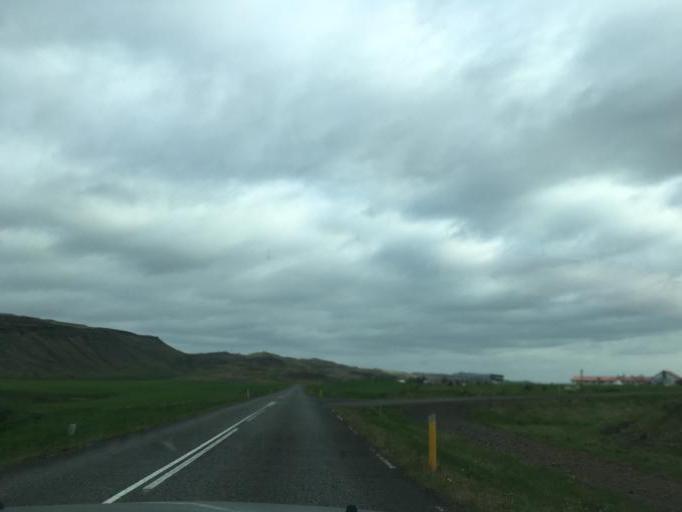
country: IS
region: South
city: Vestmannaeyjar
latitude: 64.1957
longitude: -20.2777
